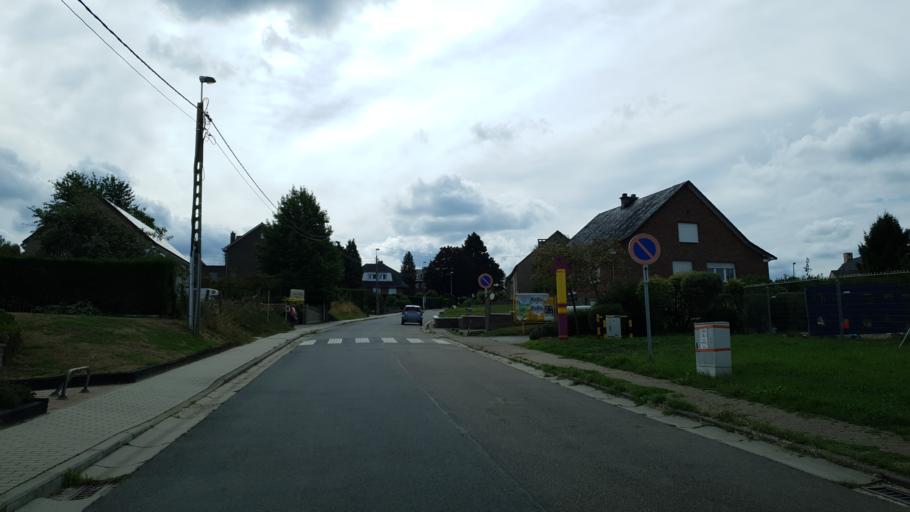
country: BE
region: Flanders
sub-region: Provincie Vlaams-Brabant
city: Herent
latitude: 50.8986
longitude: 4.6782
